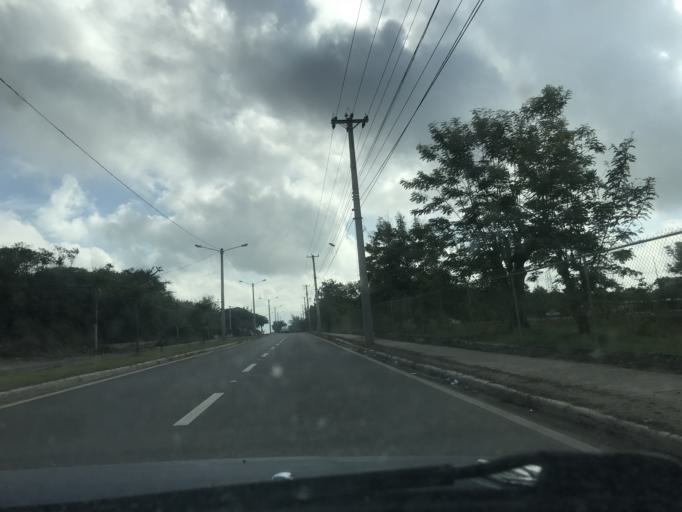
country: DO
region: Santiago
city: Santiago de los Caballeros
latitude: 19.4233
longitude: -70.7329
